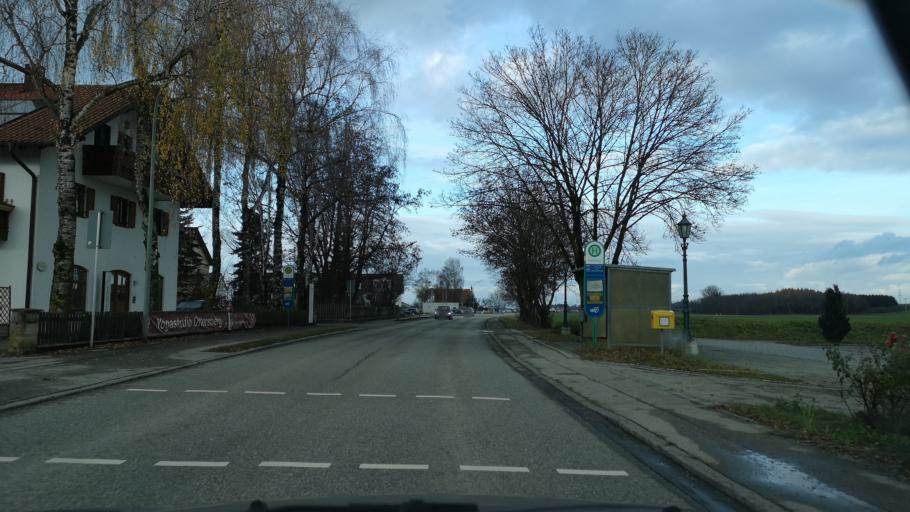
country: DE
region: Bavaria
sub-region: Upper Bavaria
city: Pliening
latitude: 48.1828
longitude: 11.8079
